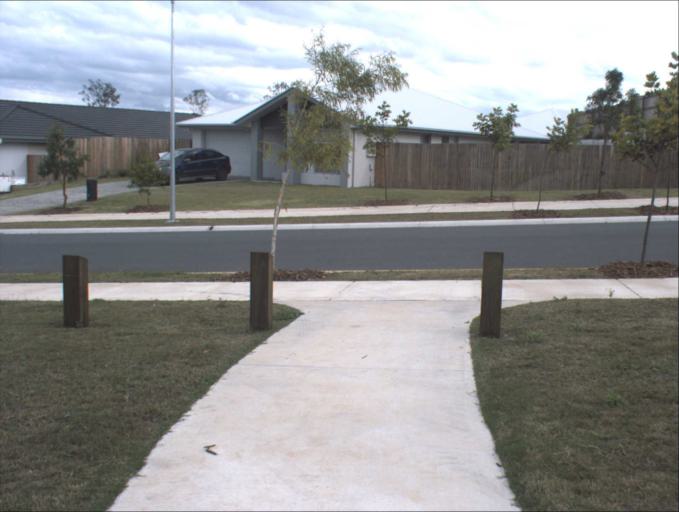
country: AU
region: Queensland
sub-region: Logan
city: Chambers Flat
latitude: -27.7979
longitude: 153.1068
